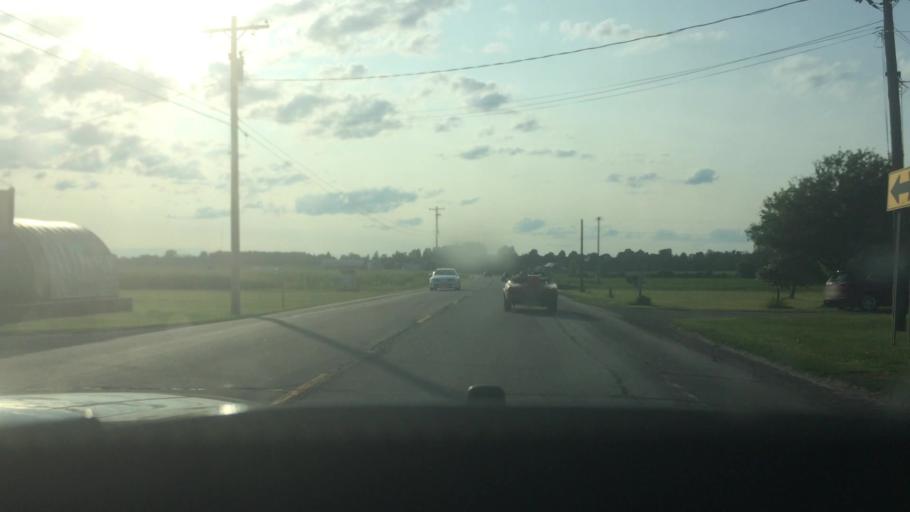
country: US
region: New York
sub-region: St. Lawrence County
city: Ogdensburg
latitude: 44.6625
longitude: -75.3414
